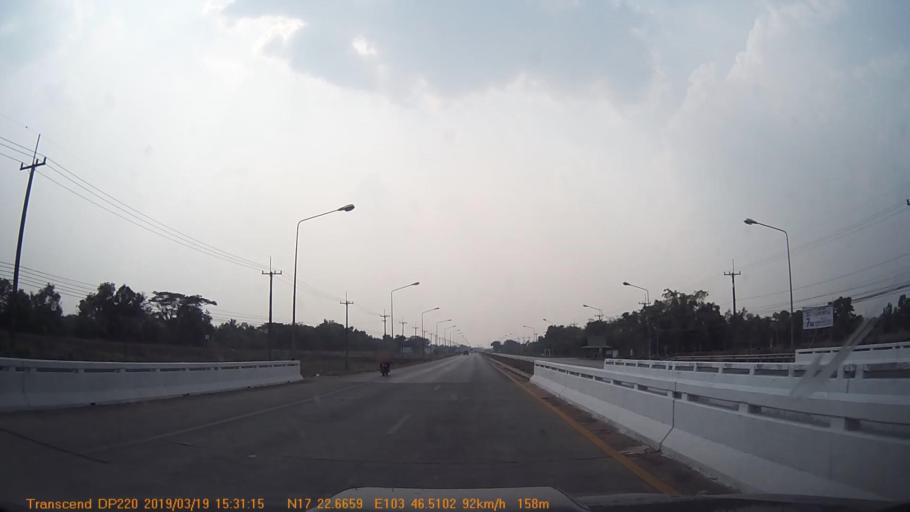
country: TH
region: Sakon Nakhon
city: Phang Khon
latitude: 17.3778
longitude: 103.7746
